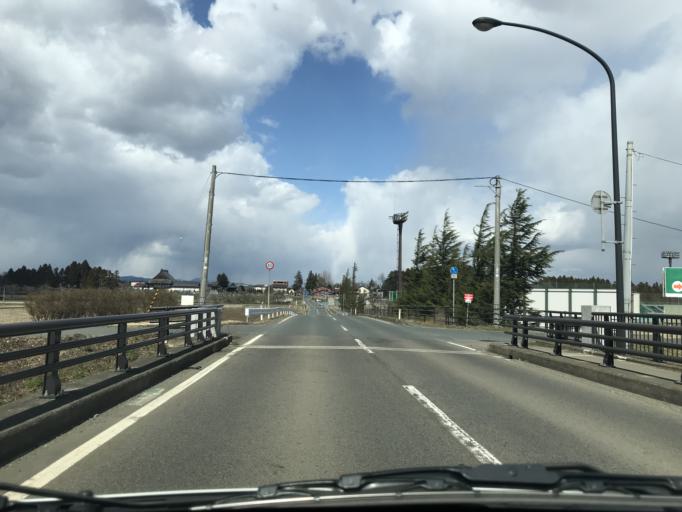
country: JP
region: Iwate
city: Kitakami
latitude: 39.2917
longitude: 141.0689
